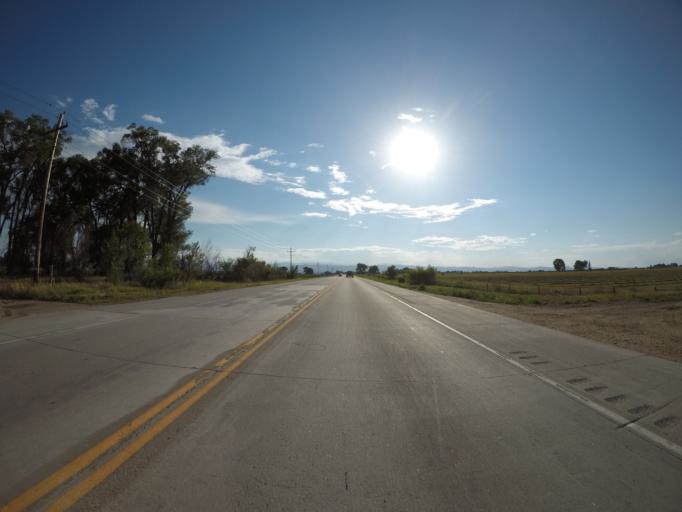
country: US
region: Colorado
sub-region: Weld County
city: Severance
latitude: 40.5813
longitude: -104.9315
